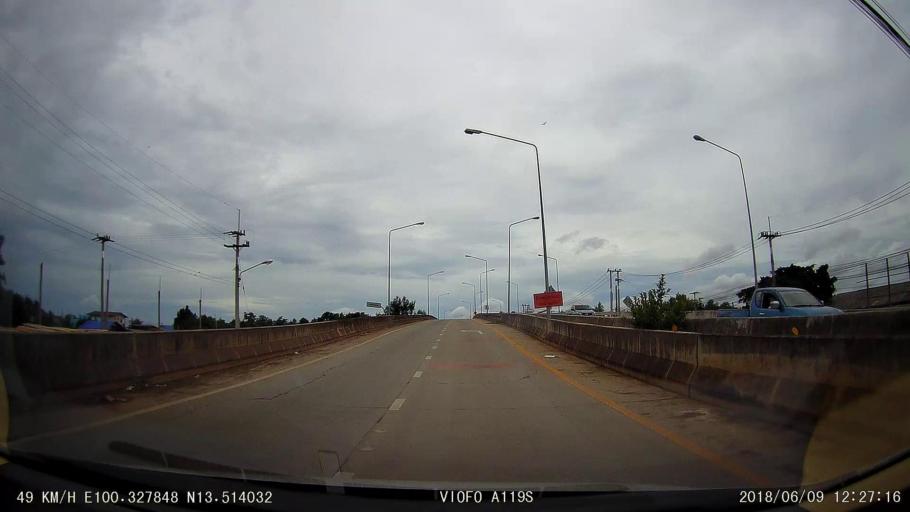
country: TH
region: Samut Sakhon
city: Samut Sakhon
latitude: 13.5141
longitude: 100.3277
